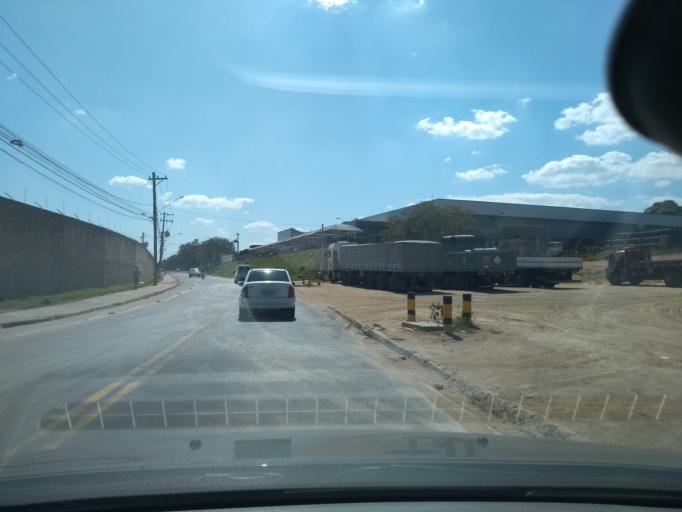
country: BR
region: Sao Paulo
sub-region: Itupeva
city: Itupeva
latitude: -23.1486
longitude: -47.0438
